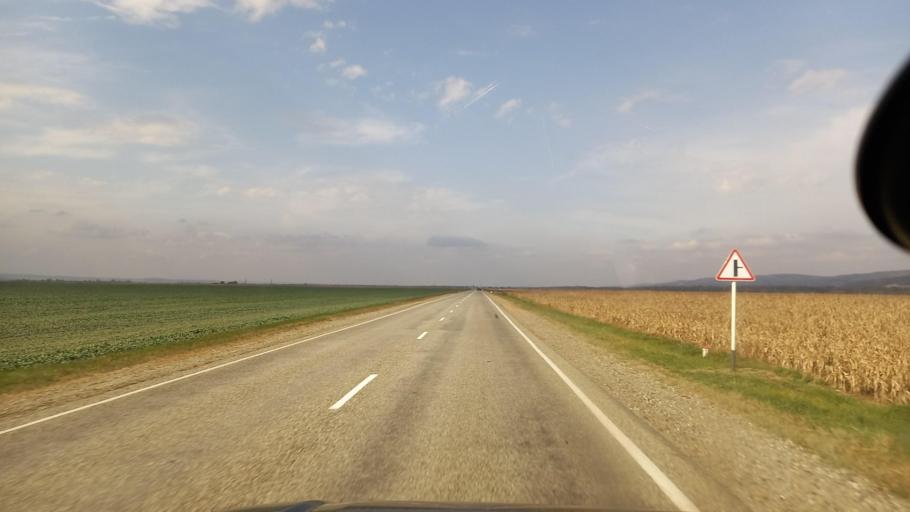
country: RU
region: Krasnodarskiy
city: Perepravnaya
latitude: 44.3078
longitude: 40.8584
